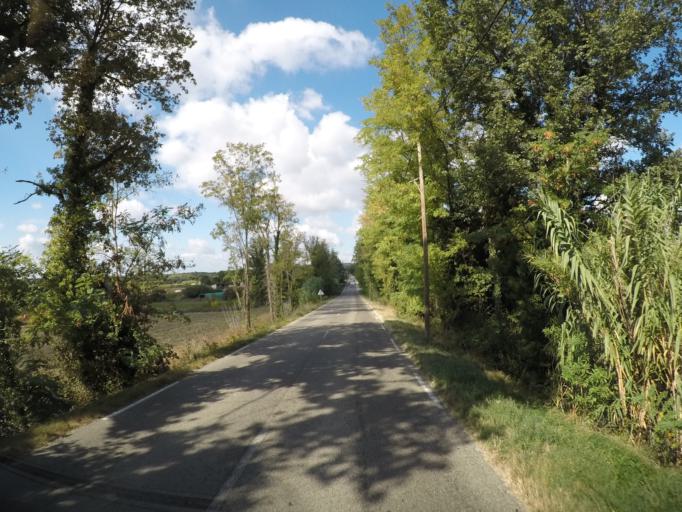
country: FR
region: Provence-Alpes-Cote d'Azur
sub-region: Departement du Vaucluse
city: Visan
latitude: 44.2871
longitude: 4.9893
